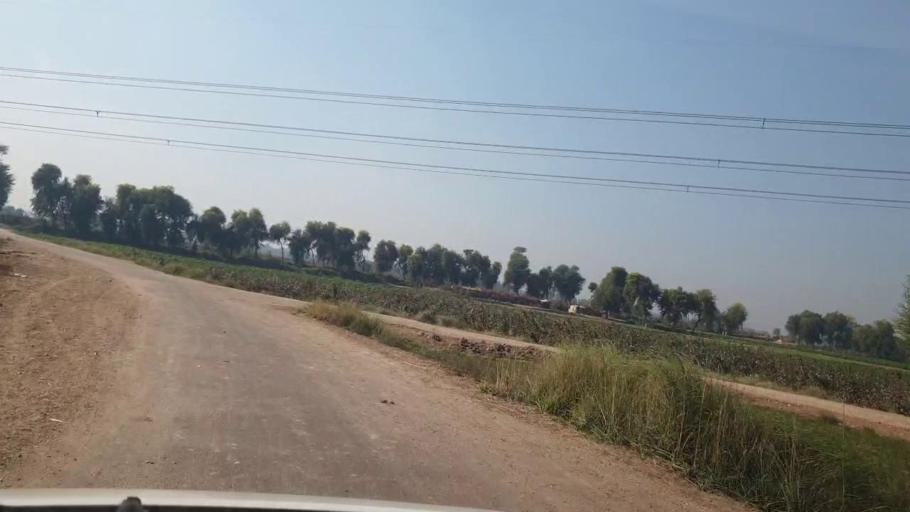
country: PK
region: Sindh
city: Bhan
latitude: 26.6066
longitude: 67.7544
